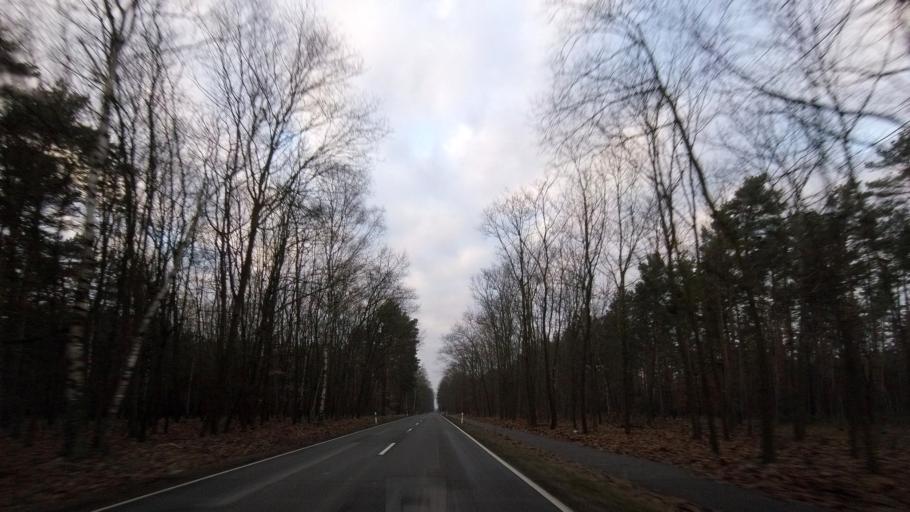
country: DE
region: Brandenburg
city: Michendorf
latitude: 52.3333
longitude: 13.0194
